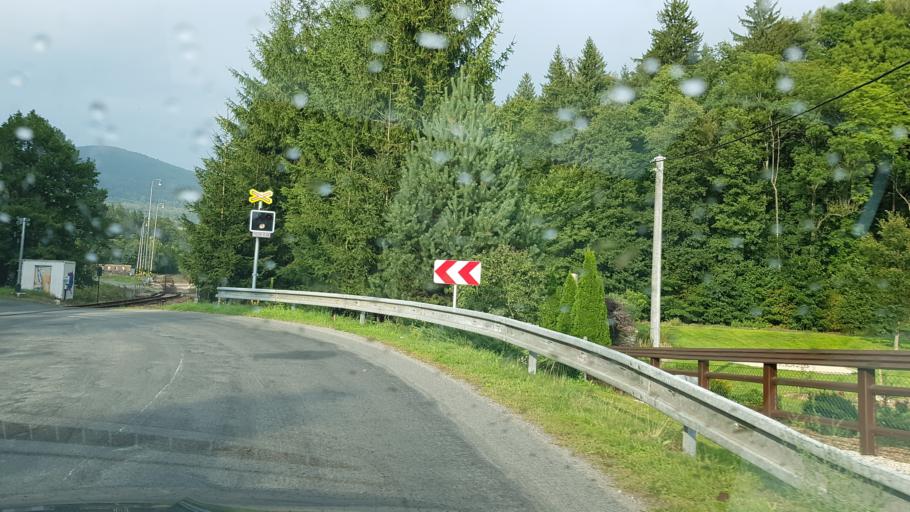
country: CZ
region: Pardubicky
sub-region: Okres Usti nad Orlici
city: Kraliky
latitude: 50.0881
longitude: 16.8475
